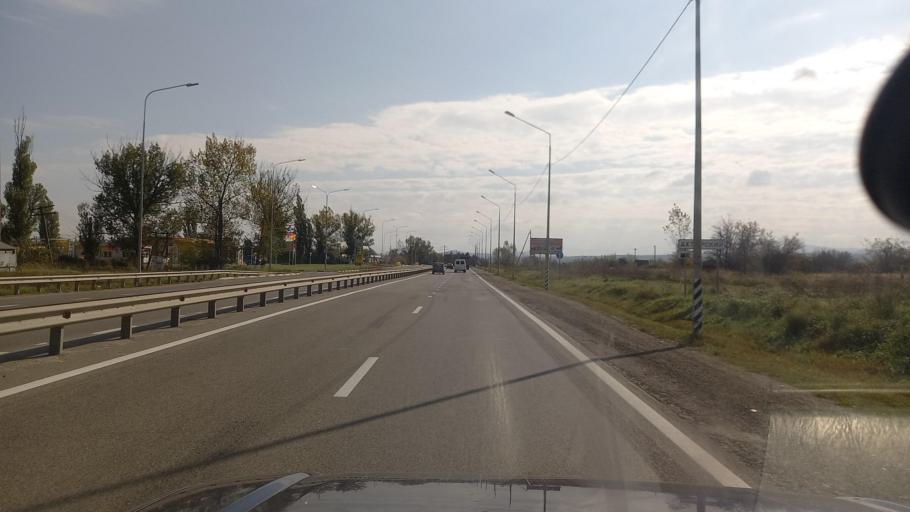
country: RU
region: Krasnodarskiy
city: Akhtyrskiy
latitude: 44.8490
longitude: 38.2756
